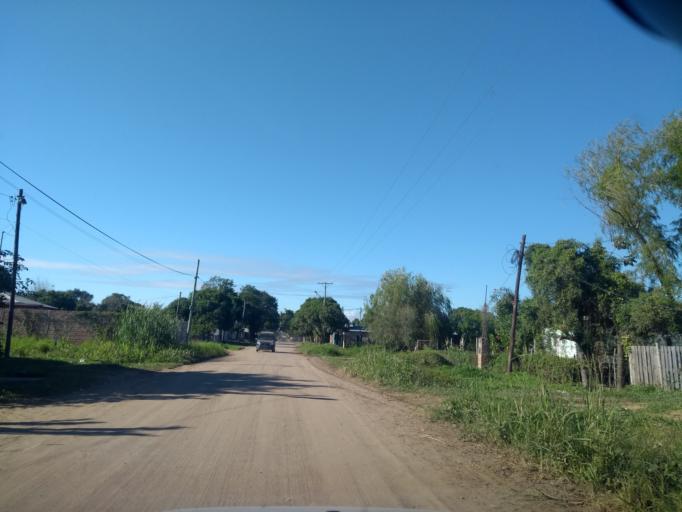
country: AR
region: Chaco
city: Barranqueras
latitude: -27.4799
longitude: -58.9303
